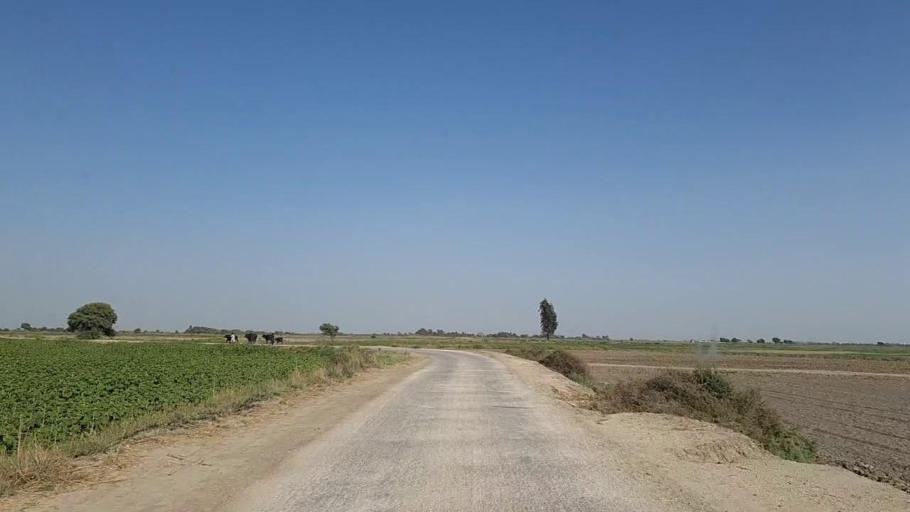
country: PK
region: Sindh
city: Chuhar Jamali
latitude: 24.5249
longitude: 68.1108
